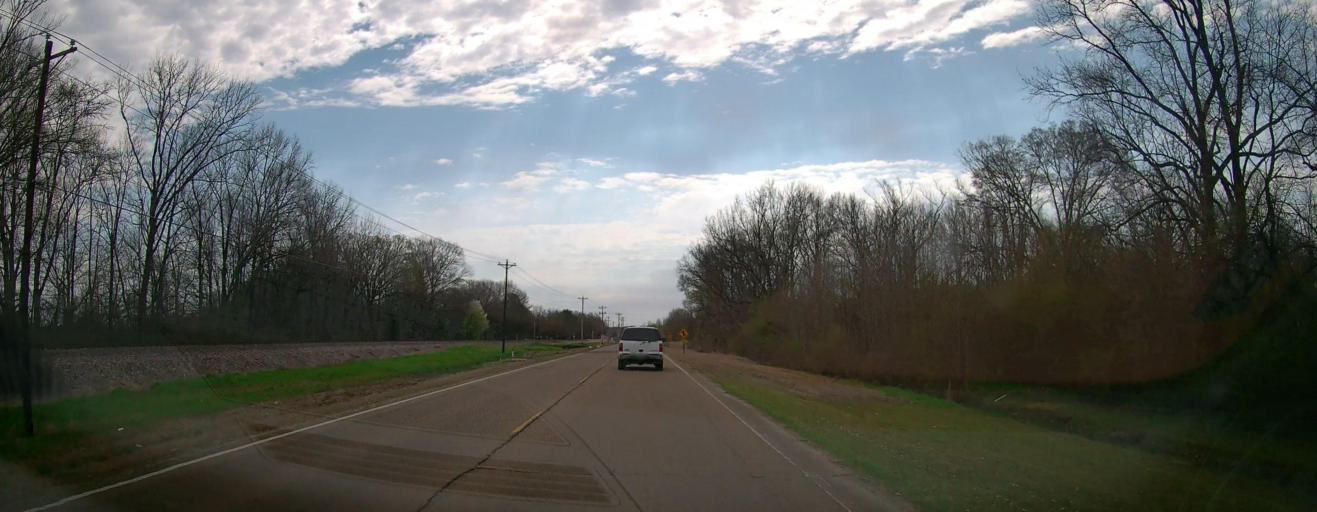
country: US
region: Mississippi
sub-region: De Soto County
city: Olive Branch
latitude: 34.9193
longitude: -89.7701
